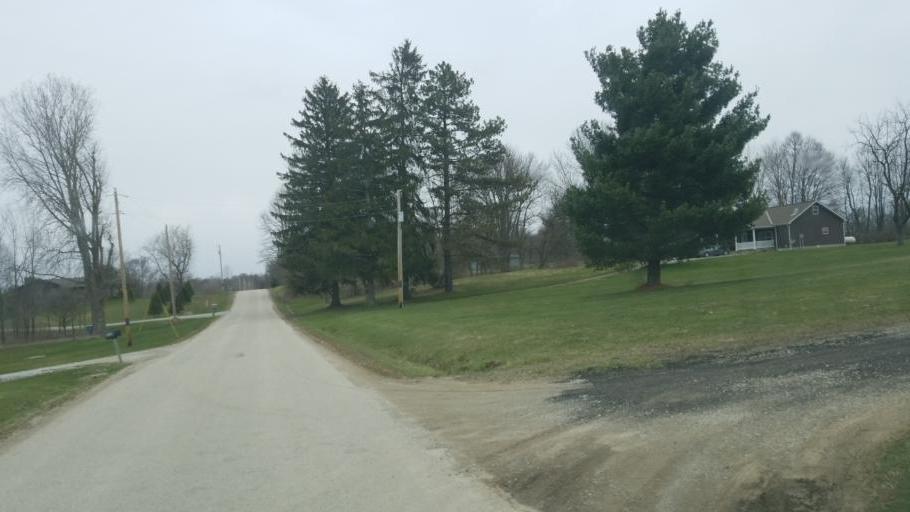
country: US
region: Ohio
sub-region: Knox County
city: Centerburg
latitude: 40.3306
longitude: -82.6476
